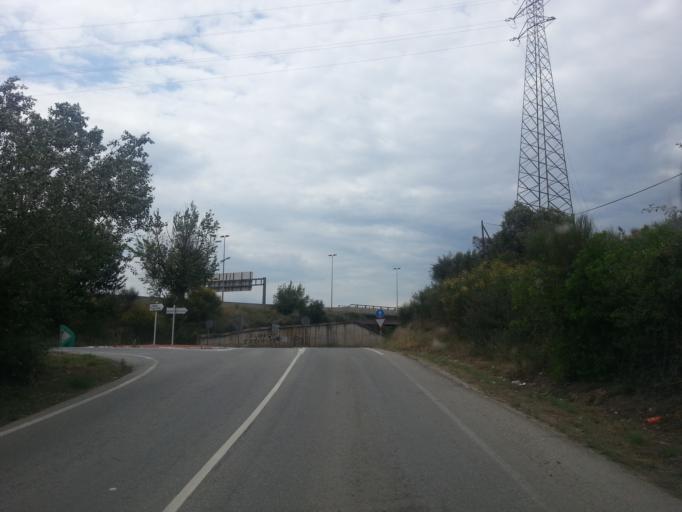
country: ES
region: Catalonia
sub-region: Provincia de Barcelona
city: Molins de Rei
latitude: 41.4217
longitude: 2.0085
